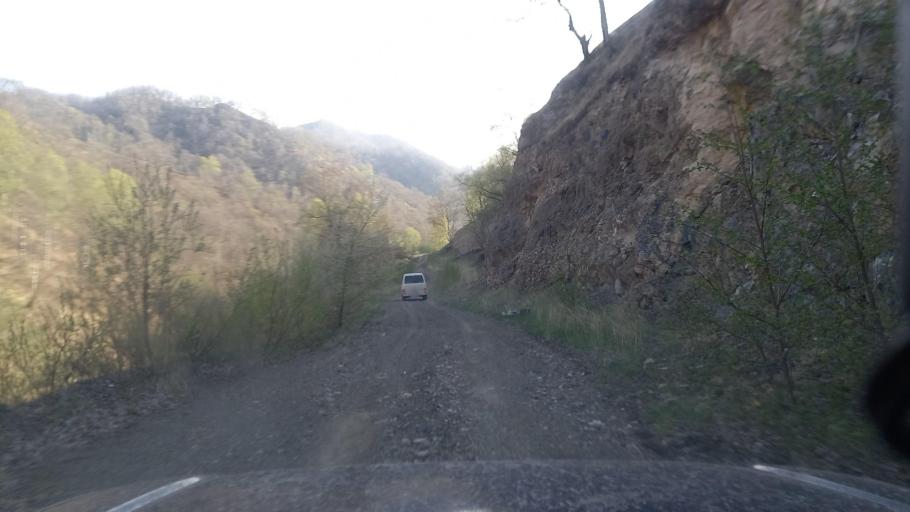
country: RU
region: Kabardino-Balkariya
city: Kamennomostskoye
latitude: 43.7001
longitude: 42.8428
